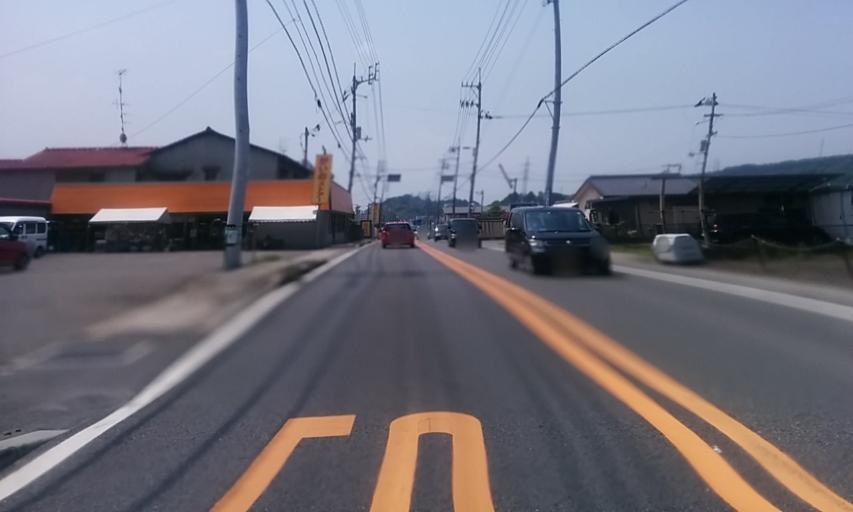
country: JP
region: Ehime
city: Niihama
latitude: 33.9290
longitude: 133.2711
